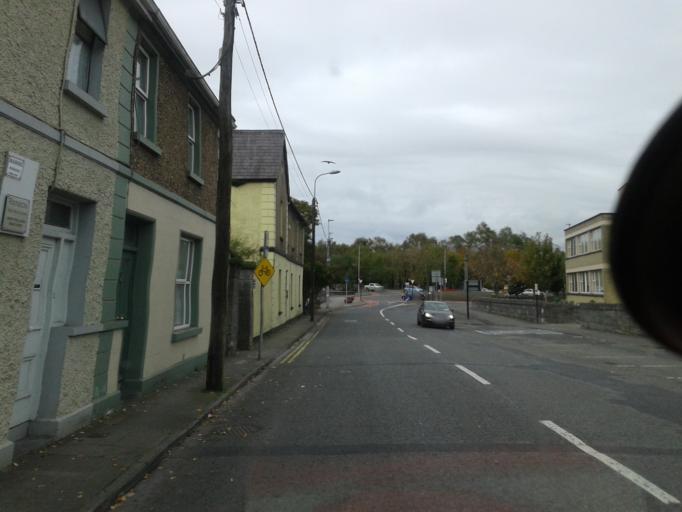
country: IE
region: Munster
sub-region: An Clar
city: Ennis
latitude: 52.8467
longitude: -8.9871
